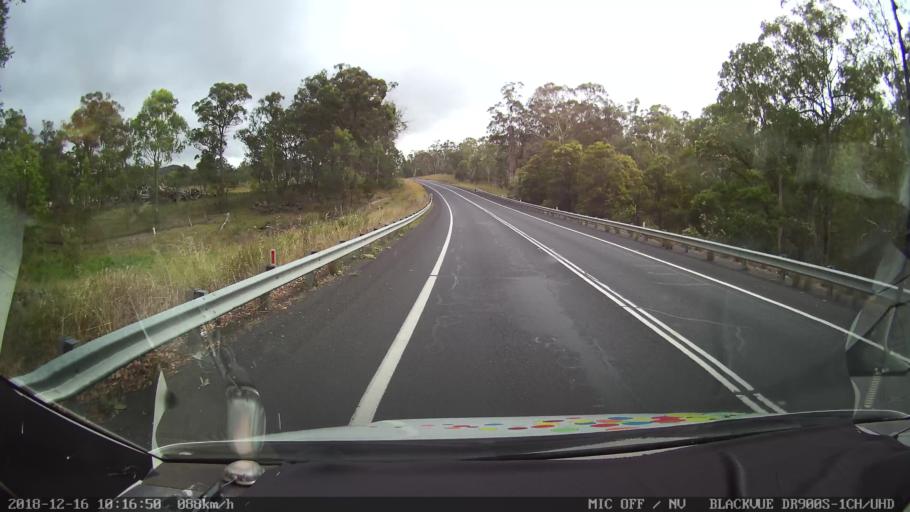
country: AU
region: New South Wales
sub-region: Tenterfield Municipality
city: Carrolls Creek
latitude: -29.2629
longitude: 151.9870
